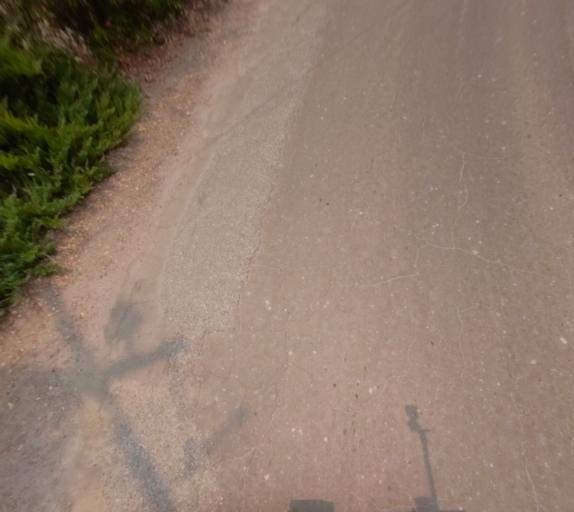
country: US
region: California
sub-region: Madera County
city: Oakhurst
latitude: 37.3388
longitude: -119.6520
